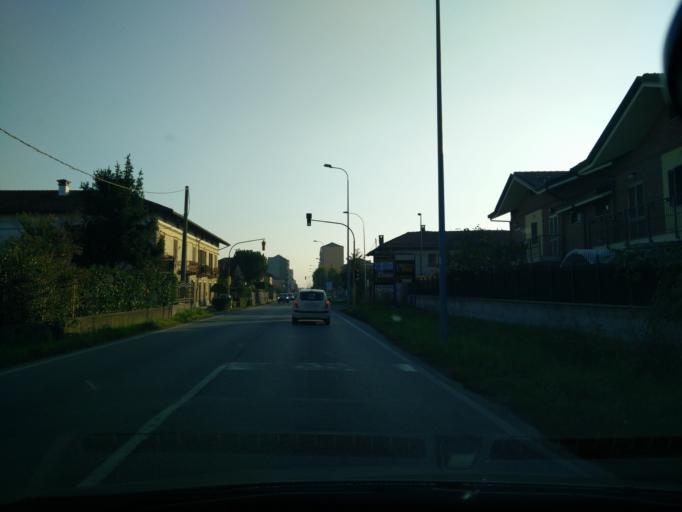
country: IT
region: Piedmont
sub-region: Provincia di Torino
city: Leini
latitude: 45.1529
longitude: 7.7087
